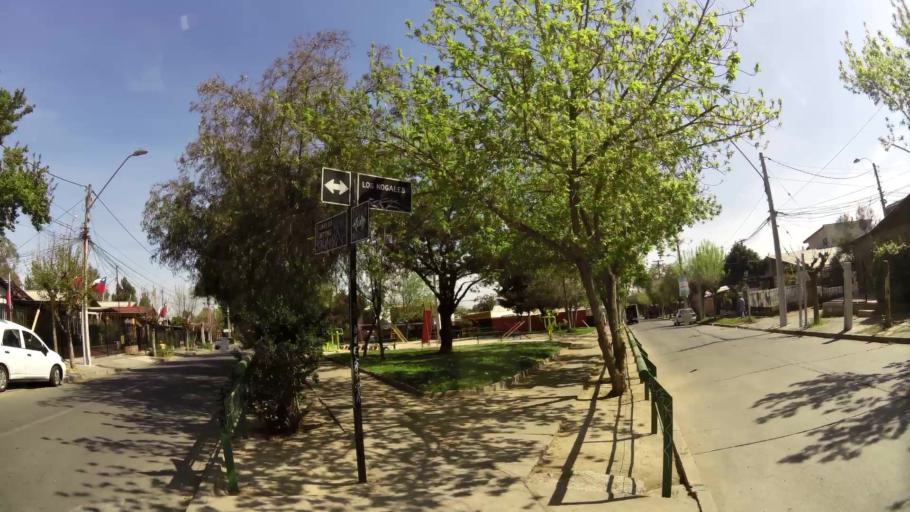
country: CL
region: Santiago Metropolitan
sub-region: Provincia de Santiago
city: Villa Presidente Frei, Nunoa, Santiago, Chile
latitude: -33.5281
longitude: -70.5622
